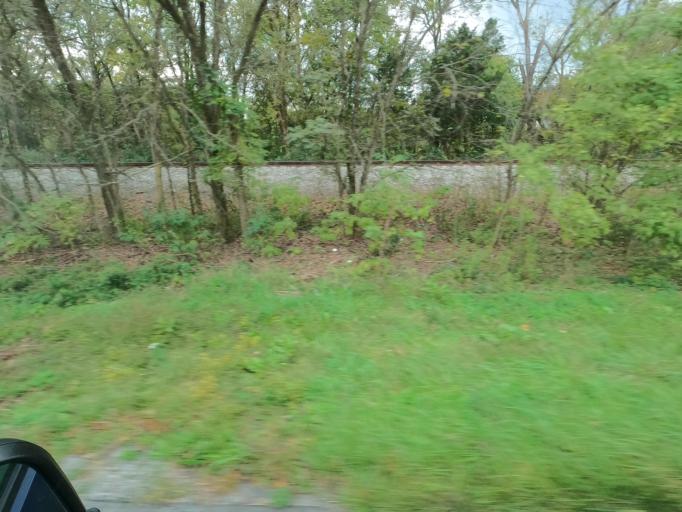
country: US
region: Tennessee
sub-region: Cheatham County
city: Pegram
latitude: 36.0963
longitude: -87.0443
